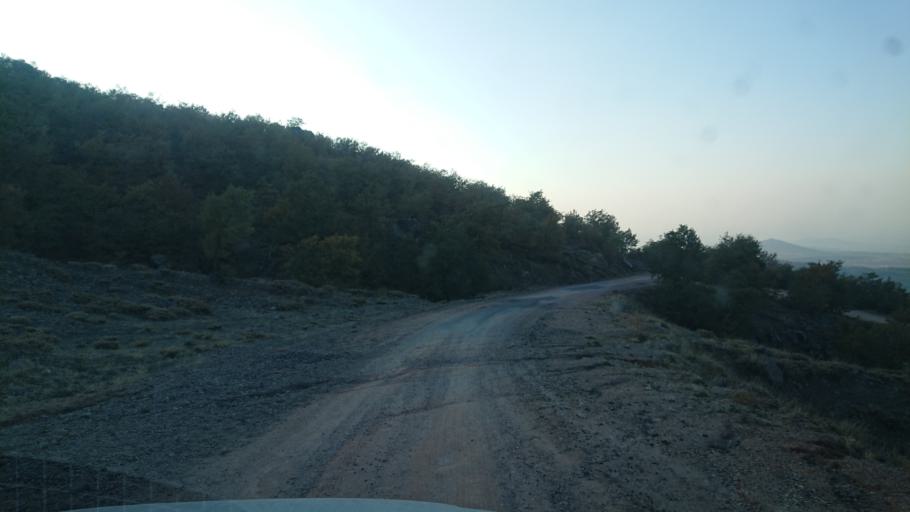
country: TR
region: Aksaray
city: Taspinar
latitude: 38.1703
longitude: 34.1804
